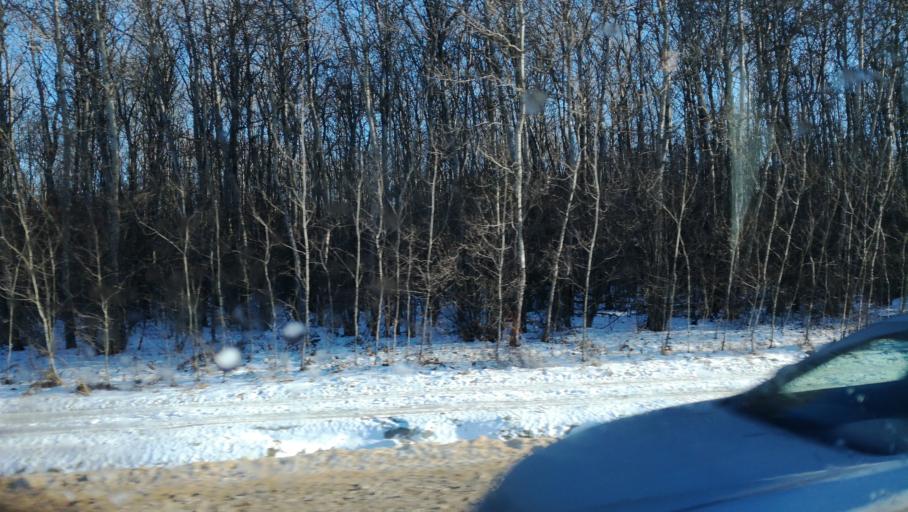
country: RU
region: Tula
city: Barsuki
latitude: 54.1726
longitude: 37.4564
